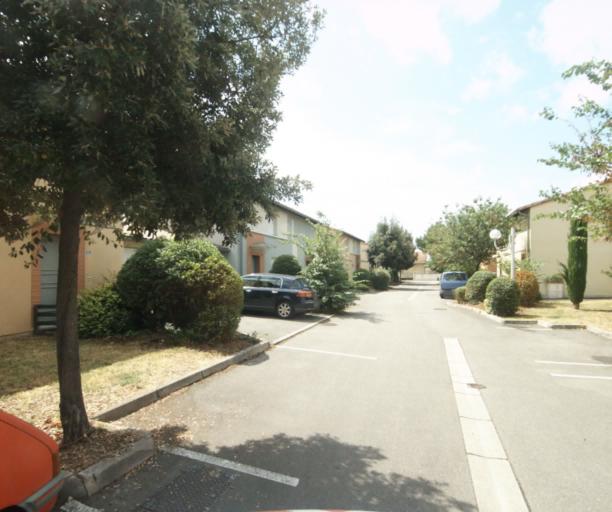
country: FR
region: Midi-Pyrenees
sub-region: Departement de la Haute-Garonne
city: Revel
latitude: 43.4641
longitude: 2.0046
